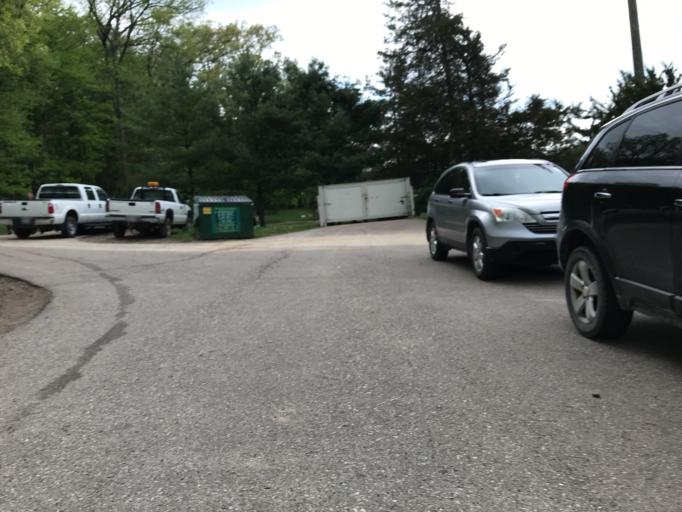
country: US
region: Michigan
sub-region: Oakland County
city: Milford
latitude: 42.5514
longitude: -83.6346
